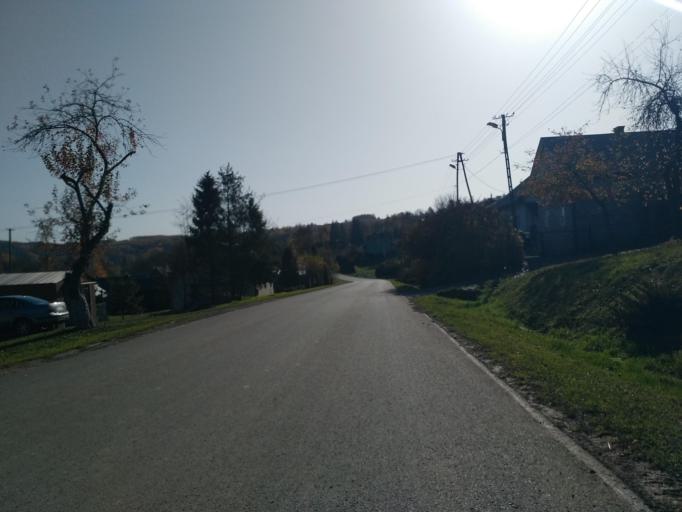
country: PL
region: Subcarpathian Voivodeship
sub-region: Powiat brzozowski
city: Nozdrzec
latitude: 49.8002
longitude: 22.1731
